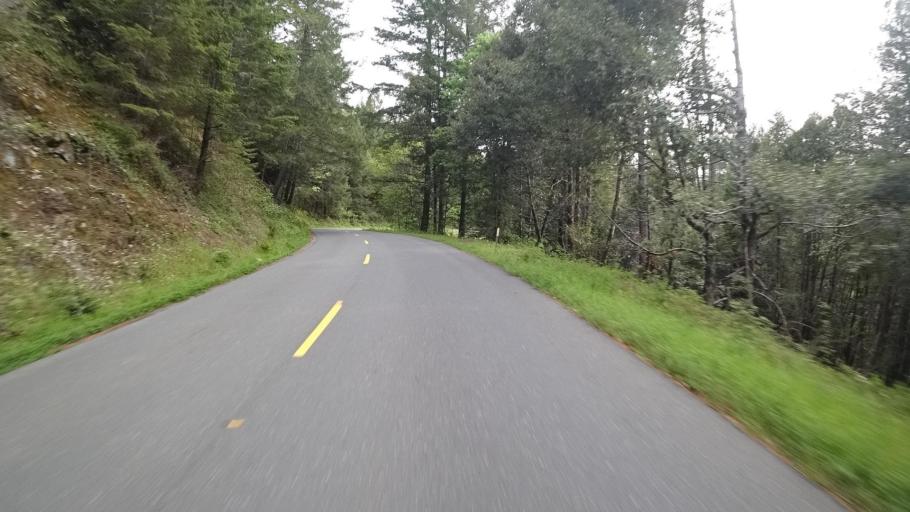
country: US
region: California
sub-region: Humboldt County
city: Redway
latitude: 40.2815
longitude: -123.8466
